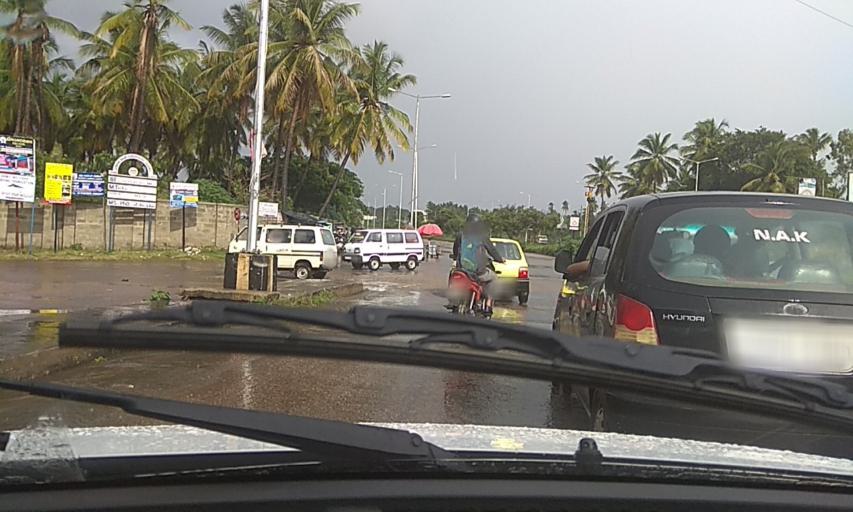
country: IN
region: Karnataka
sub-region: Mysore
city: Mysore
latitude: 12.3488
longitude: 76.6666
